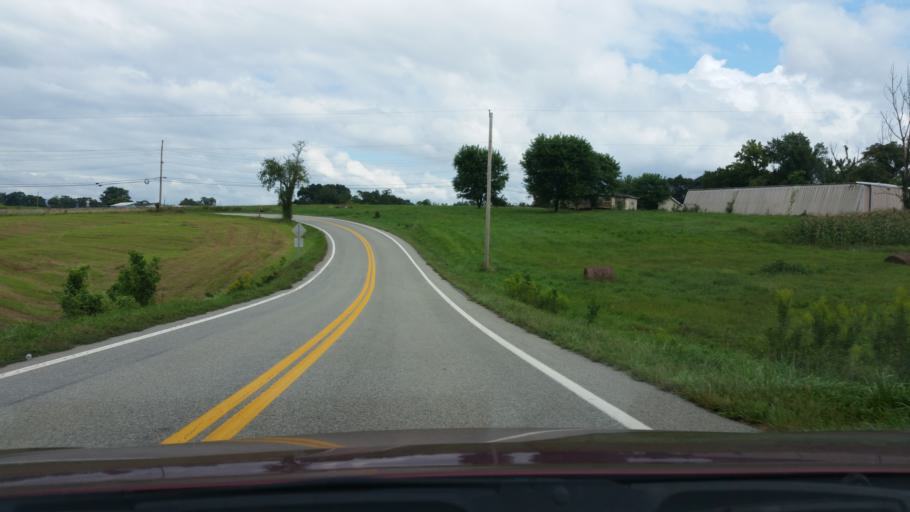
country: US
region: Maryland
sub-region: Washington County
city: Hancock
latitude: 39.6364
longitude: -78.1345
